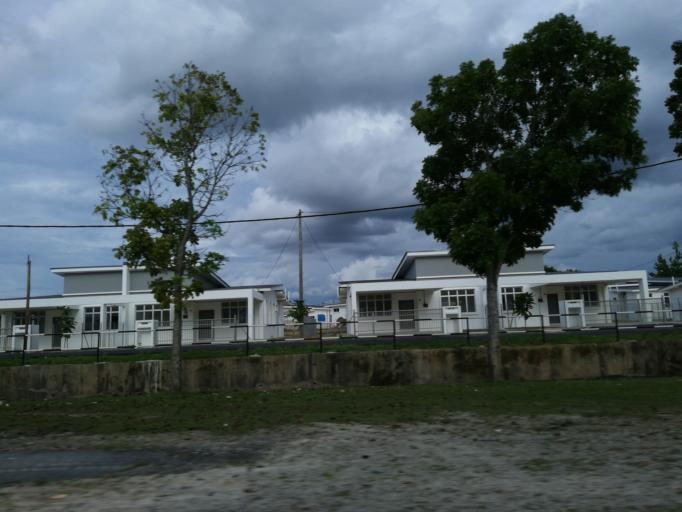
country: MY
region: Penang
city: Tasek Glugor
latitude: 5.5004
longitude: 100.6242
